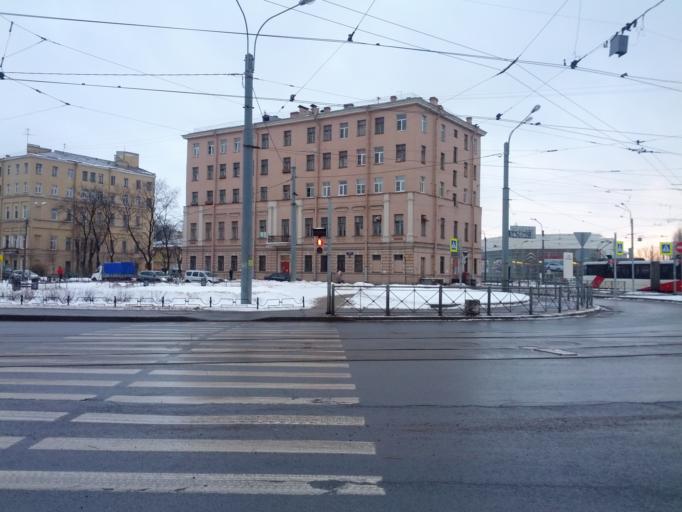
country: RU
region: St.-Petersburg
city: Centralniy
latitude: 59.9058
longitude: 30.3551
